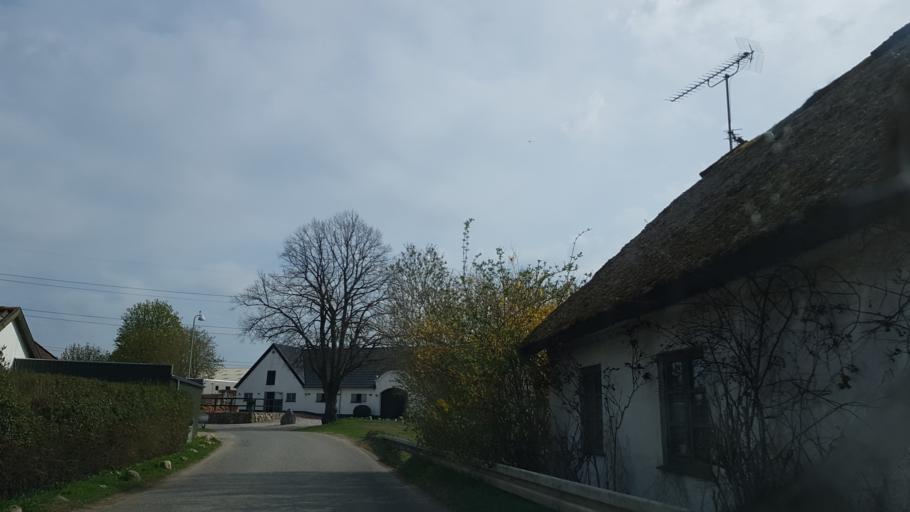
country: DK
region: Capital Region
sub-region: Allerod Kommune
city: Lillerod
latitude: 55.8912
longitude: 12.3286
